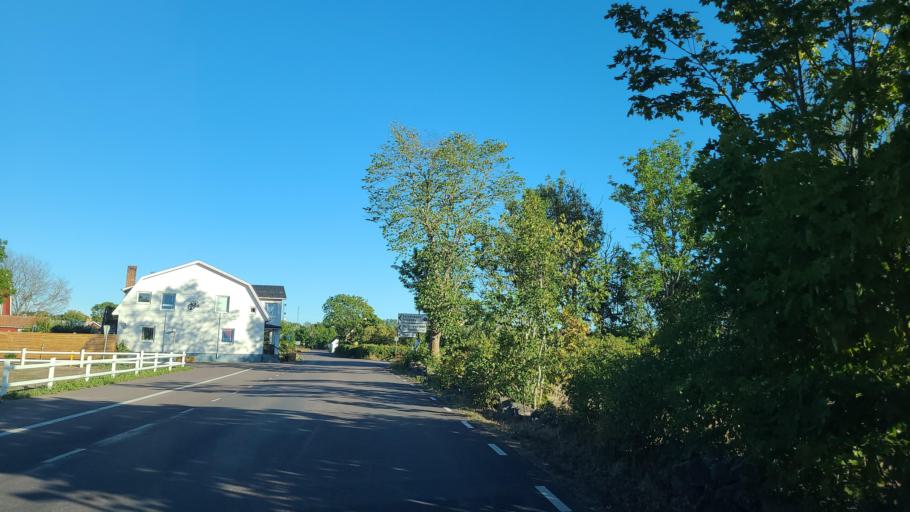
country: SE
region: Kalmar
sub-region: Borgholms Kommun
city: Borgholm
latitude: 57.3178
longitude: 17.0167
